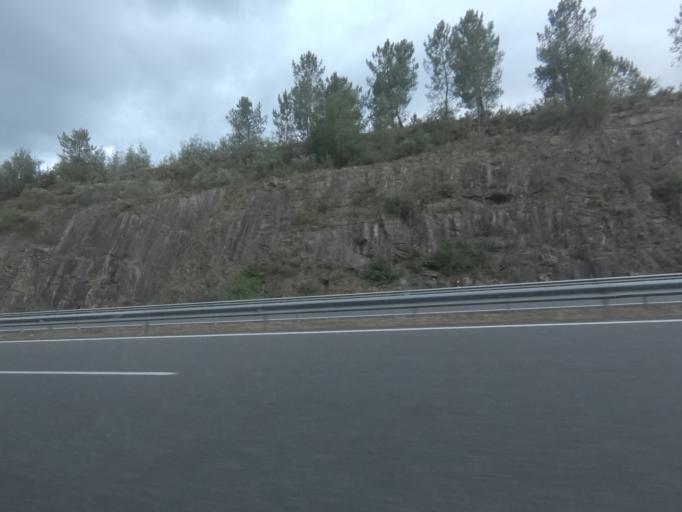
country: ES
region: Galicia
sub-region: Provincia de Ourense
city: Carballeda de Avia
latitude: 42.3066
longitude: -8.1556
